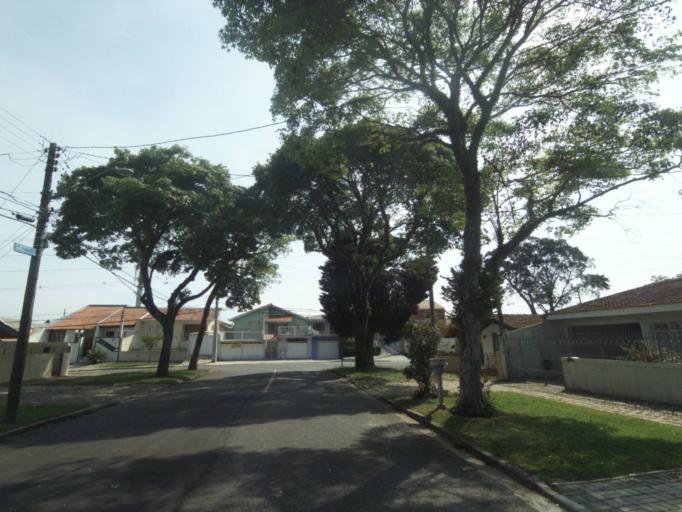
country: BR
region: Parana
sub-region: Curitiba
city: Curitiba
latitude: -25.4614
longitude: -49.3093
